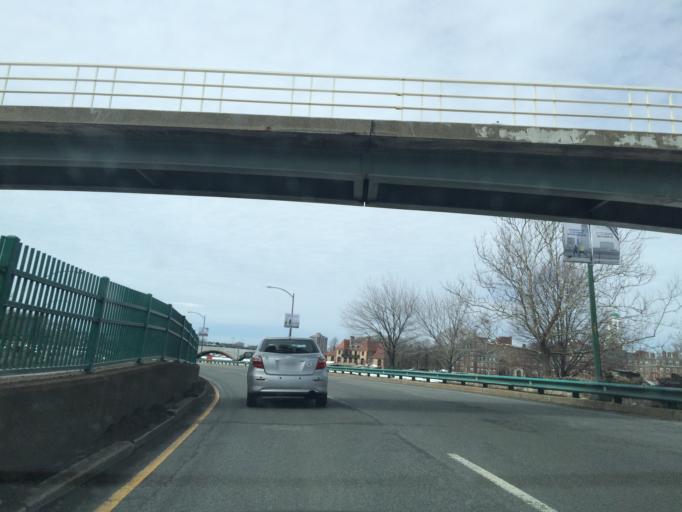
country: US
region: Massachusetts
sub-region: Middlesex County
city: Cambridge
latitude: 42.3675
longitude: -71.1189
